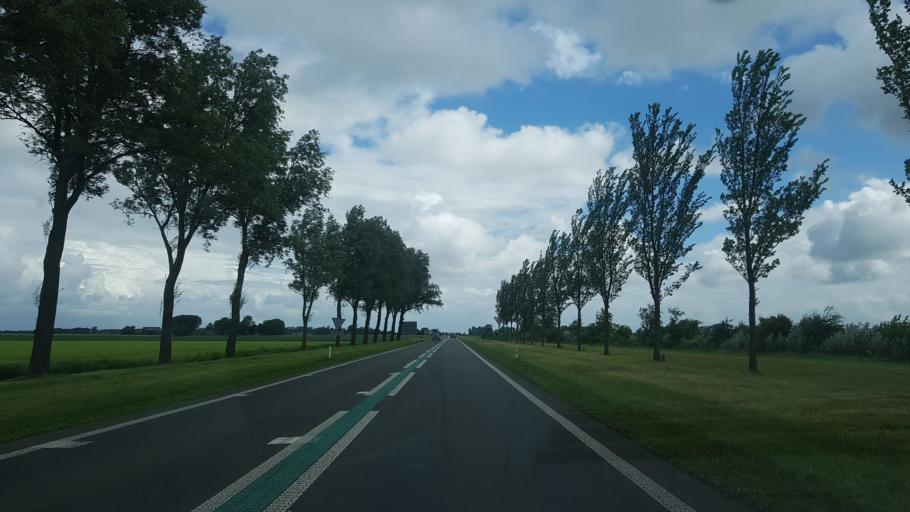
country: NL
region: Friesland
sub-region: Gemeente Dongeradeel
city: Anjum
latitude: 53.3590
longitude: 6.0764
